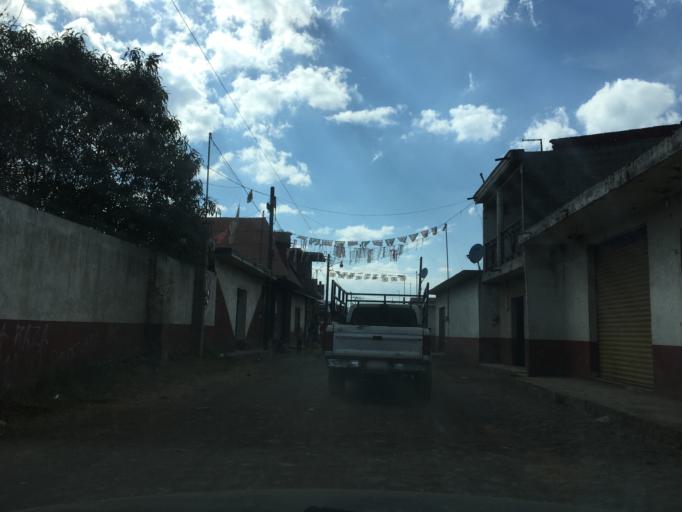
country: MX
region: Michoacan
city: Angahuan
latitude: 19.5479
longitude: -102.2273
